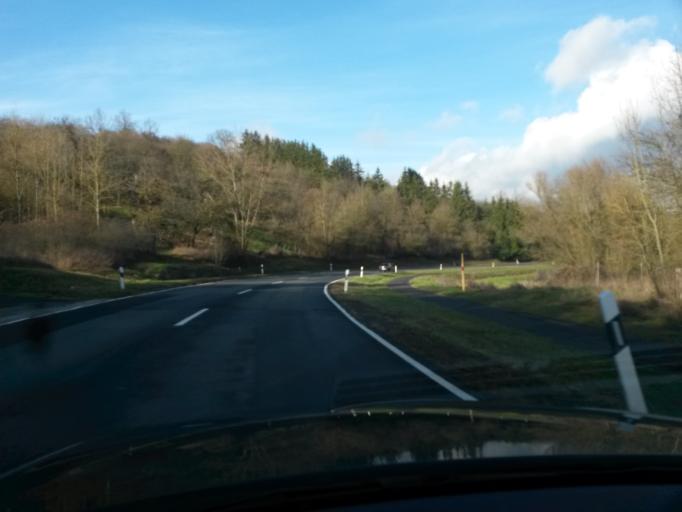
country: DE
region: Bavaria
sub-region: Regierungsbezirk Unterfranken
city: Rimpar
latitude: 49.8429
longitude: 9.9569
